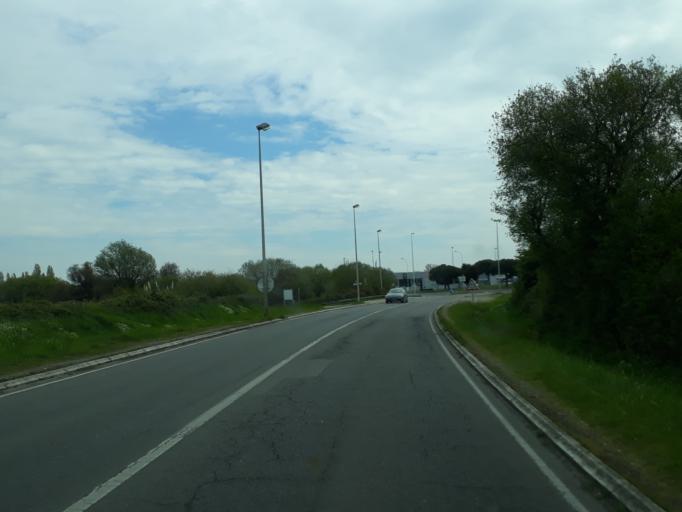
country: FR
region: Pays de la Loire
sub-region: Departement de la Loire-Atlantique
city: La Baule-Escoublac
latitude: 47.2952
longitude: -2.4000
